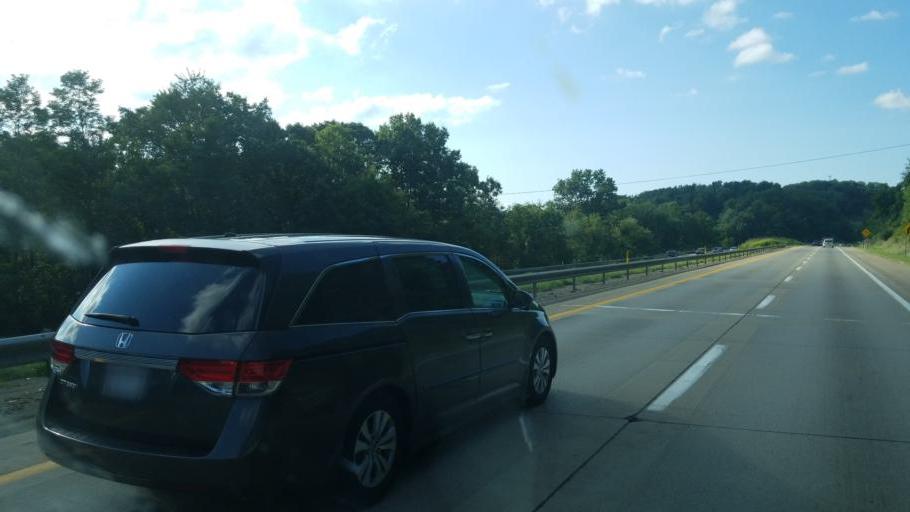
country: US
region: Pennsylvania
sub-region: Greene County
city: Waynesburg
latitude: 39.9948
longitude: -80.1867
